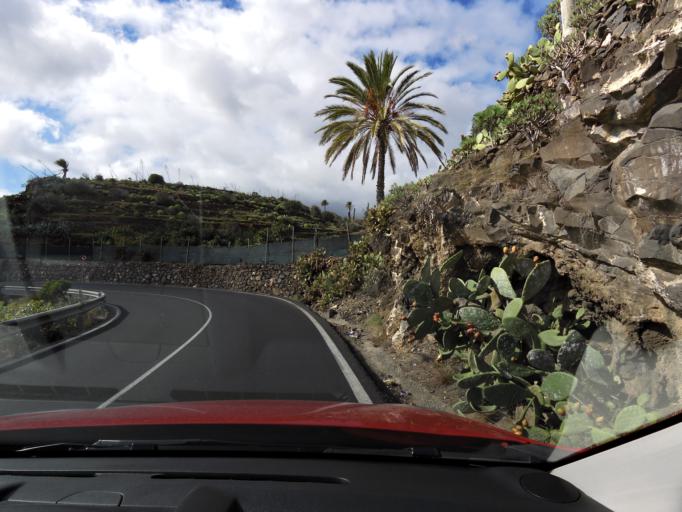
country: ES
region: Canary Islands
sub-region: Provincia de Las Palmas
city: Aguimes
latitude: 27.9096
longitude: -15.4433
